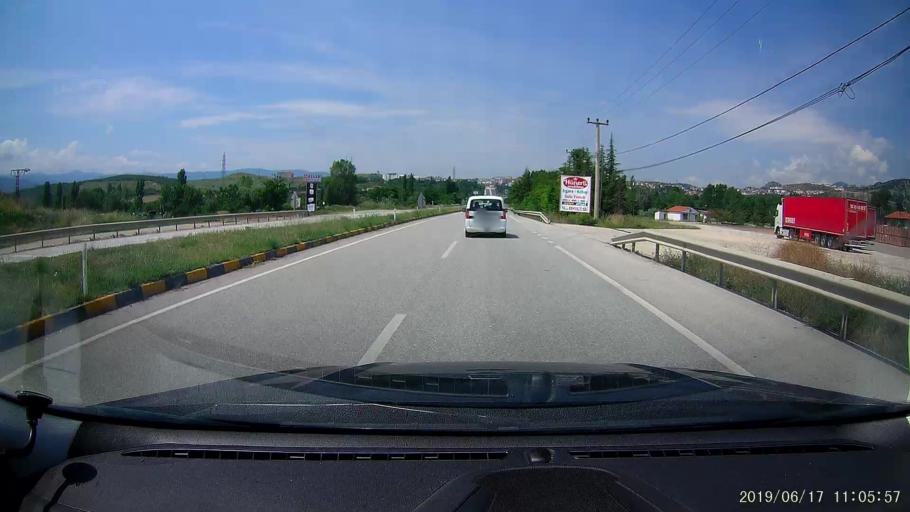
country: TR
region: Kastamonu
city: Tosya
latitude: 41.0173
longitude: 34.0744
